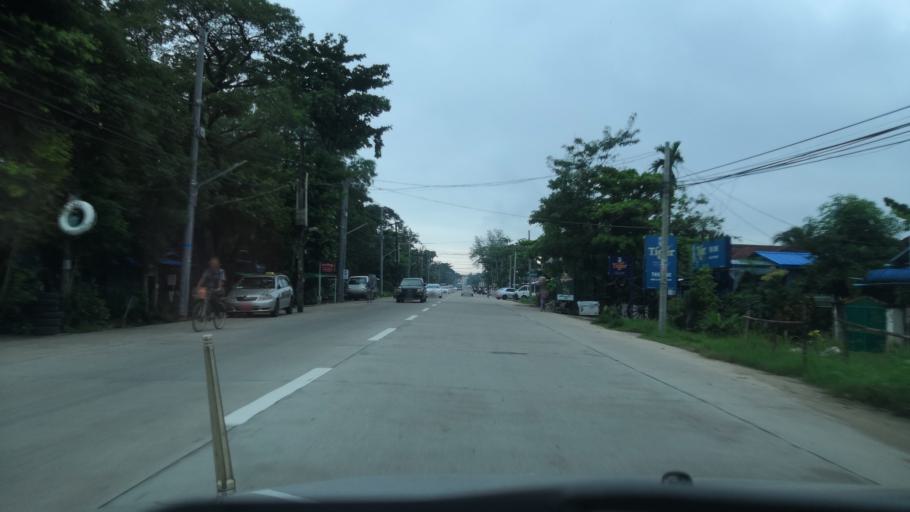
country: MM
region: Yangon
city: Yangon
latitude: 16.8807
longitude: 96.1701
